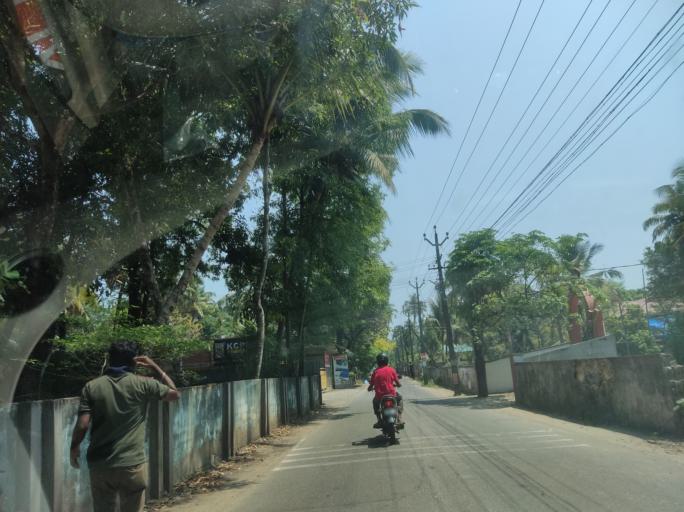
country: IN
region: Kerala
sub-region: Alappuzha
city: Kutiatodu
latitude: 9.7905
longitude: 76.3031
